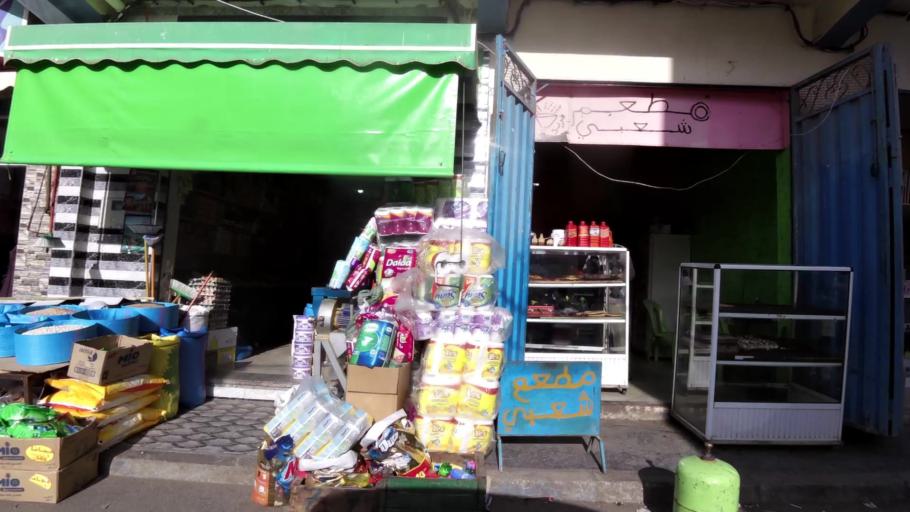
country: MA
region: Tanger-Tetouan
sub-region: Tetouan
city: Martil
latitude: 35.6128
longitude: -5.2732
